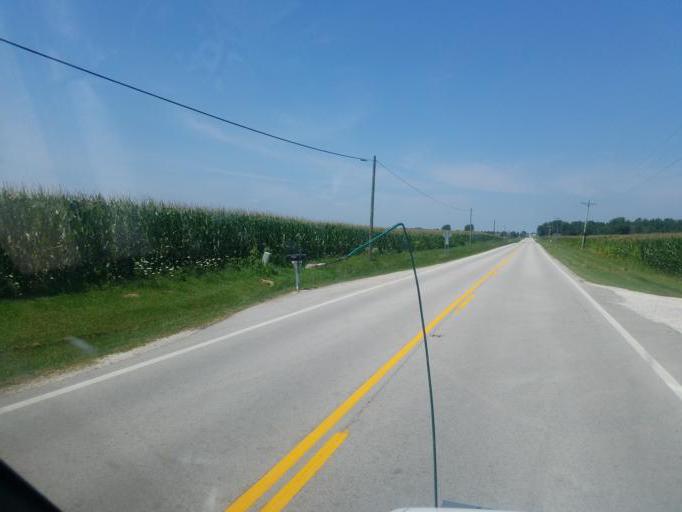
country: US
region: Ohio
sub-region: Shelby County
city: Fort Loramie
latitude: 40.3562
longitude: -84.4342
